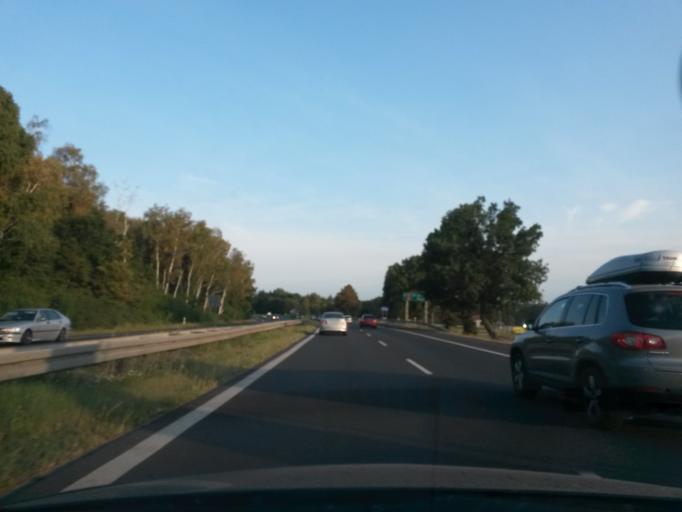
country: PL
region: Masovian Voivodeship
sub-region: Powiat nowodworski
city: Zakroczym
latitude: 52.4564
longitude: 20.5798
